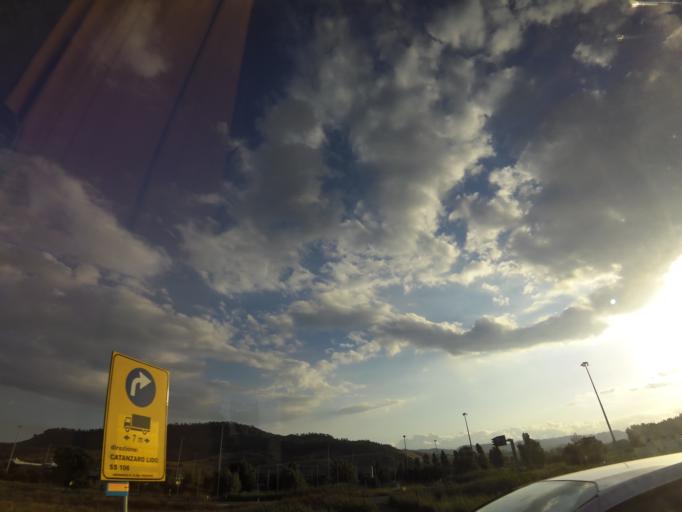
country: IT
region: Calabria
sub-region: Provincia di Catanzaro
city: Catanzaro
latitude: 38.8580
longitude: 16.5721
